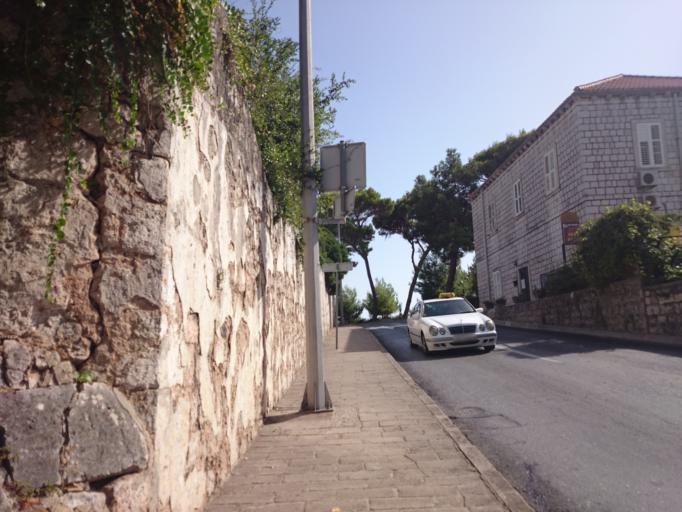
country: HR
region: Dubrovacko-Neretvanska
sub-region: Grad Dubrovnik
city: Dubrovnik
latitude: 42.6468
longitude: 18.0952
